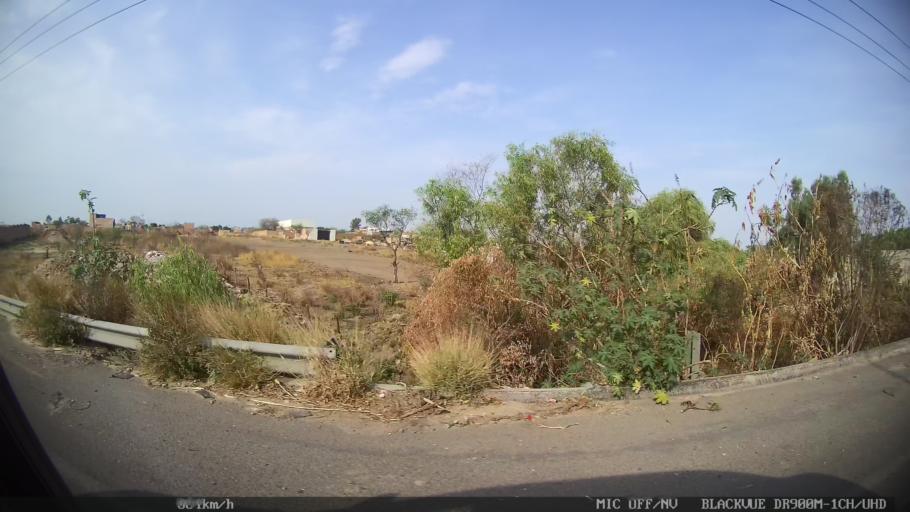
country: MX
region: Jalisco
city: Coyula
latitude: 20.6610
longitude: -103.2169
